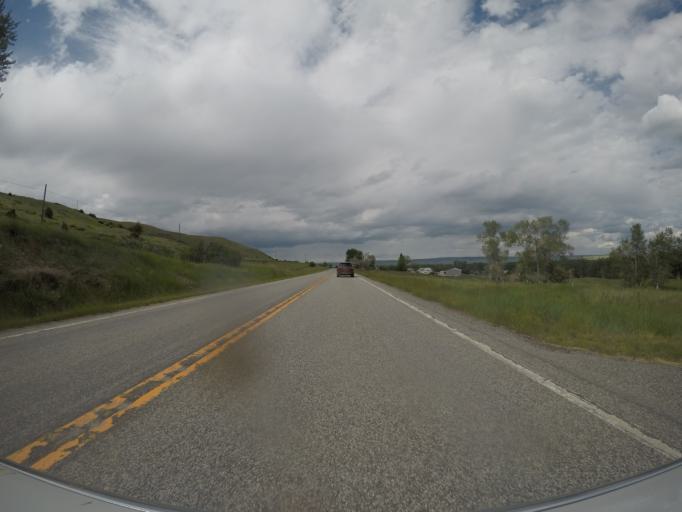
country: US
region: Montana
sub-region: Sweet Grass County
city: Big Timber
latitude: 45.8146
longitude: -109.9579
